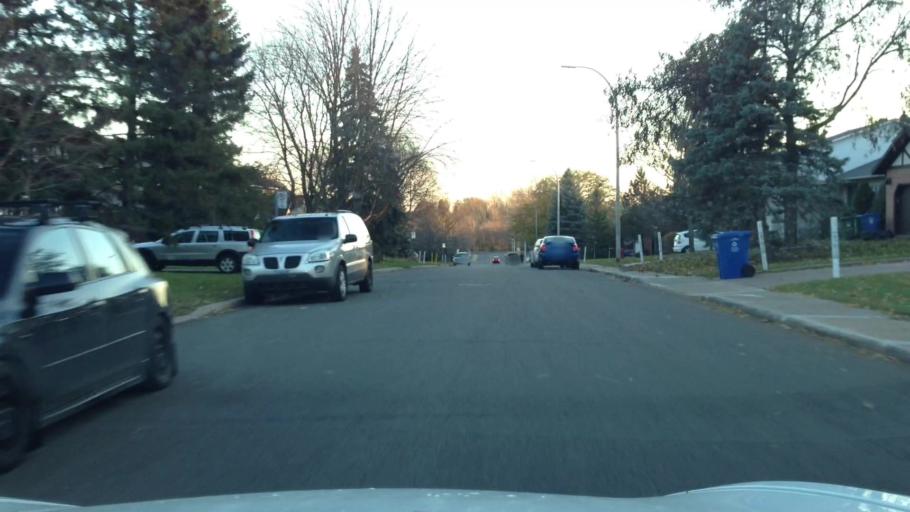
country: CA
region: Quebec
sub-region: Montreal
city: Pointe-Claire
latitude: 45.4420
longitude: -73.8340
